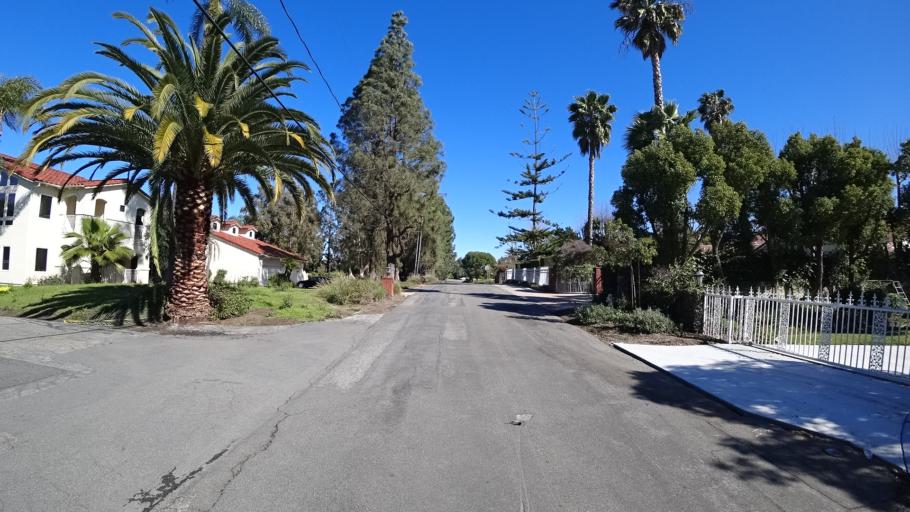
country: US
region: California
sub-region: Orange County
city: Villa Park
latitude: 33.8464
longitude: -117.8153
